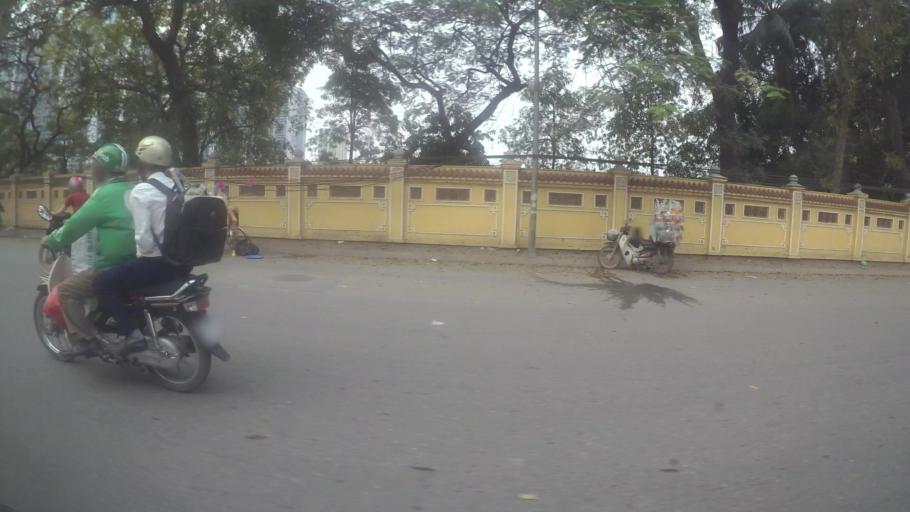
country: VN
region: Ha Noi
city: Cau Dien
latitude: 21.0394
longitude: 105.7688
